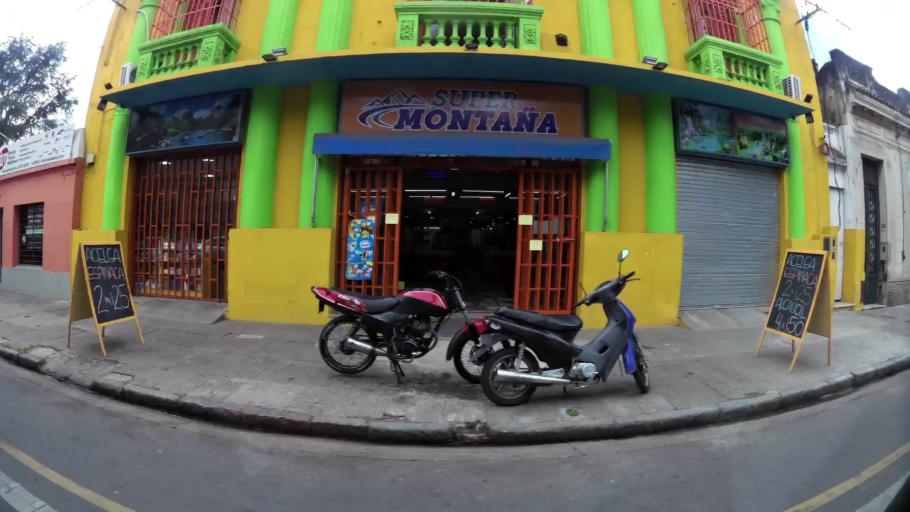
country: AR
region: Santa Fe
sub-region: Departamento de Rosario
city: Rosario
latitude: -32.9759
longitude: -60.6352
